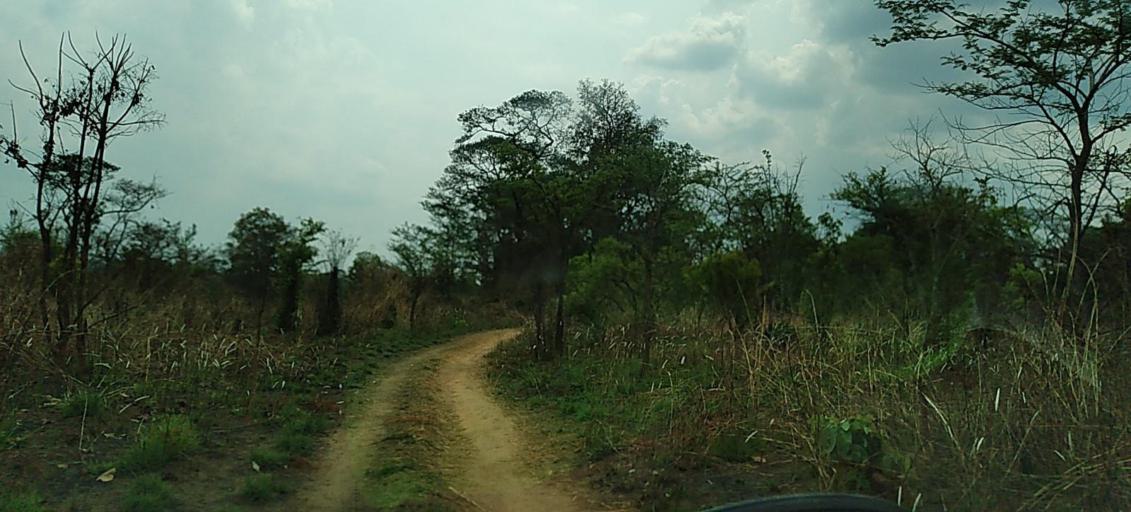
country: ZM
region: North-Western
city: Solwezi
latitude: -12.7952
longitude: 26.5304
